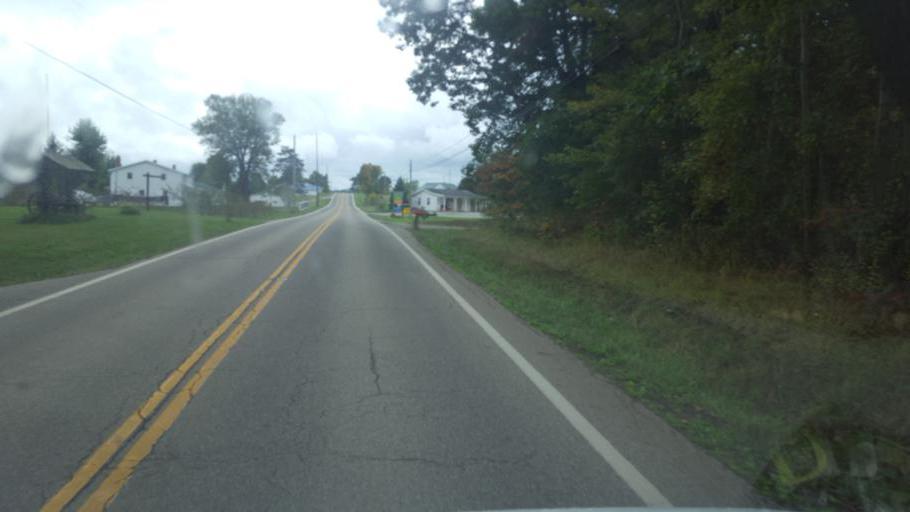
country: US
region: Ohio
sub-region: Wayne County
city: Shreve
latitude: 40.6319
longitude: -82.0783
